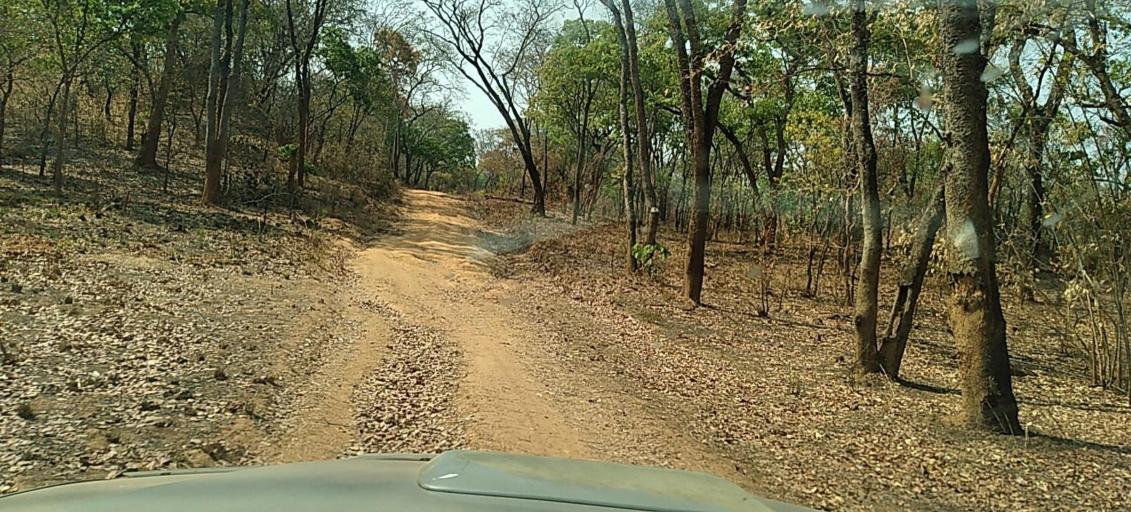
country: ZM
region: North-Western
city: Kasempa
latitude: -13.5336
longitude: 26.4083
